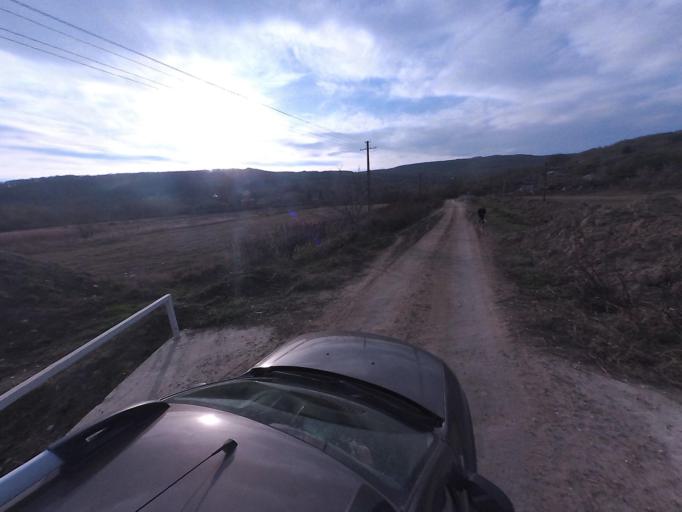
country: RO
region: Vaslui
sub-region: Comuna Gherghesti
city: Gherghesti
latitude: 46.4908
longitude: 27.5318
